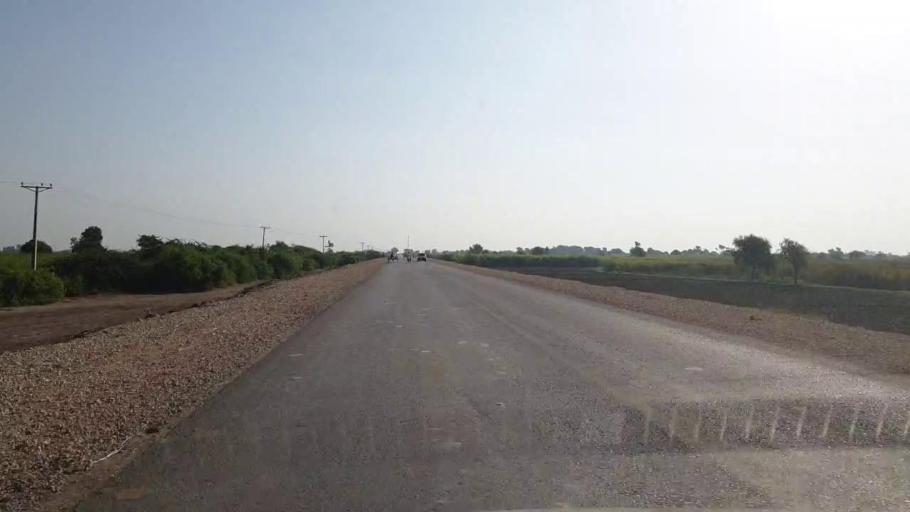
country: PK
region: Sindh
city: Badin
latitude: 24.6589
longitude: 68.9330
